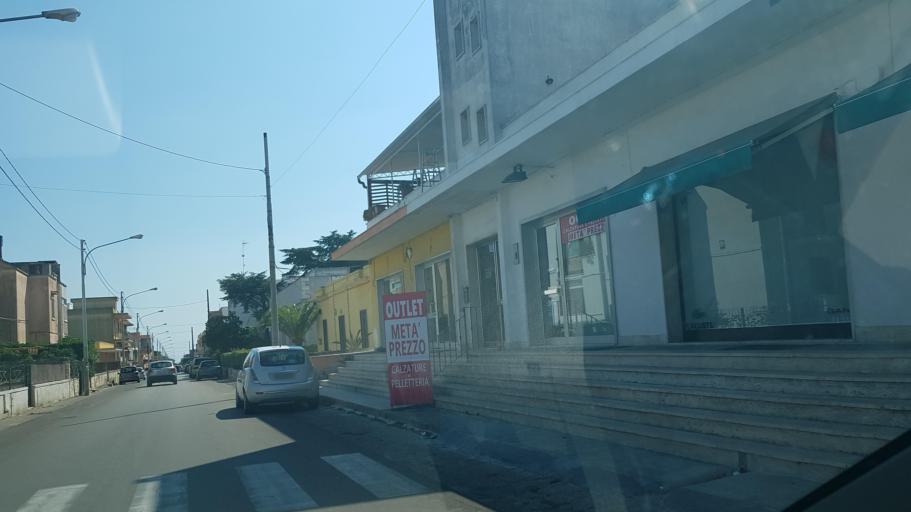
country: IT
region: Apulia
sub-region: Provincia di Lecce
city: Ugento
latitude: 39.9245
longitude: 18.1590
